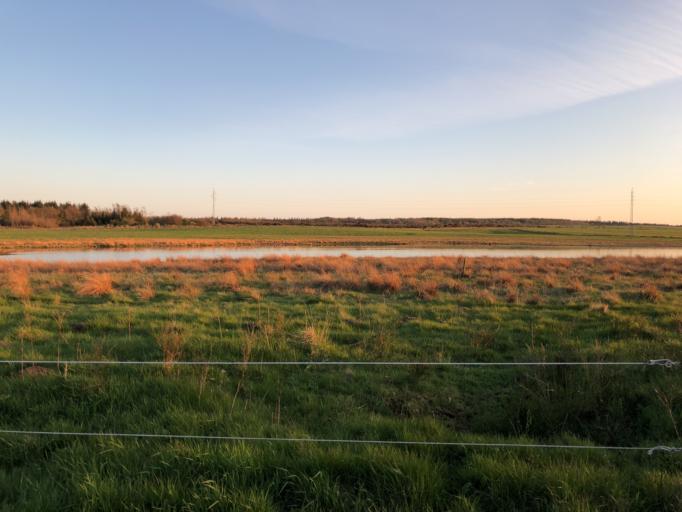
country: DK
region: Central Jutland
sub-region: Holstebro Kommune
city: Ulfborg
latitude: 56.2483
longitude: 8.4089
